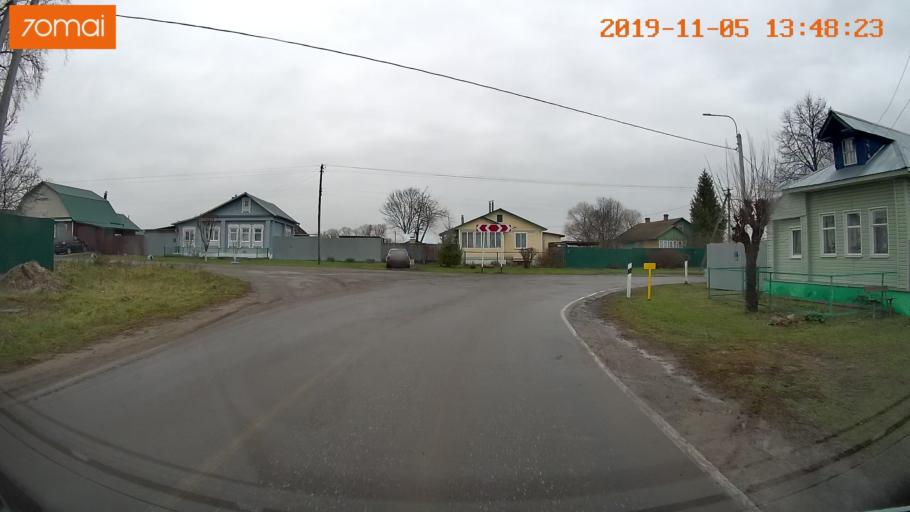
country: RU
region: Ivanovo
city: Shuya
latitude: 57.0039
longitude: 41.4059
